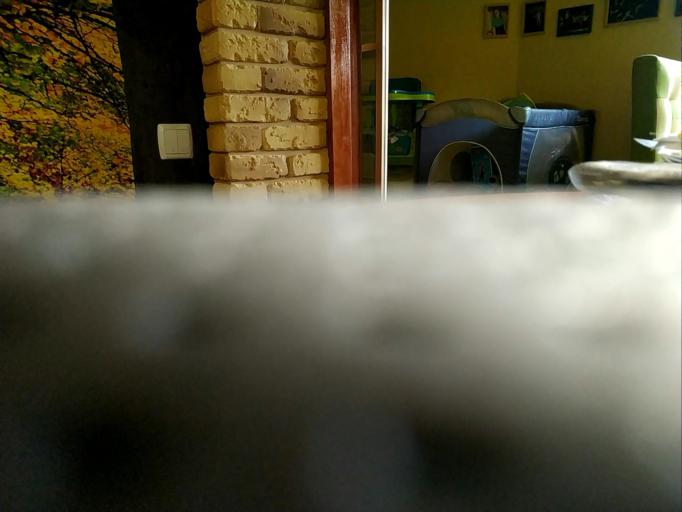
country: RU
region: Kaluga
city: Seredeyskiy
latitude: 53.8852
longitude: 35.3610
